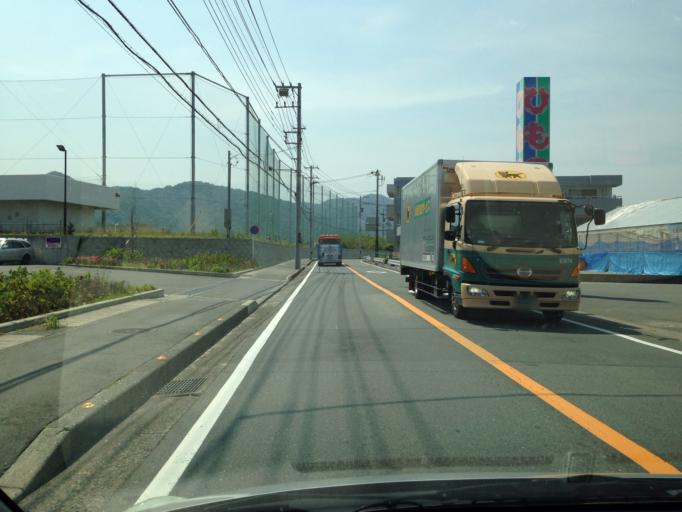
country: JP
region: Shizuoka
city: Numazu
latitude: 35.0500
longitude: 138.8858
